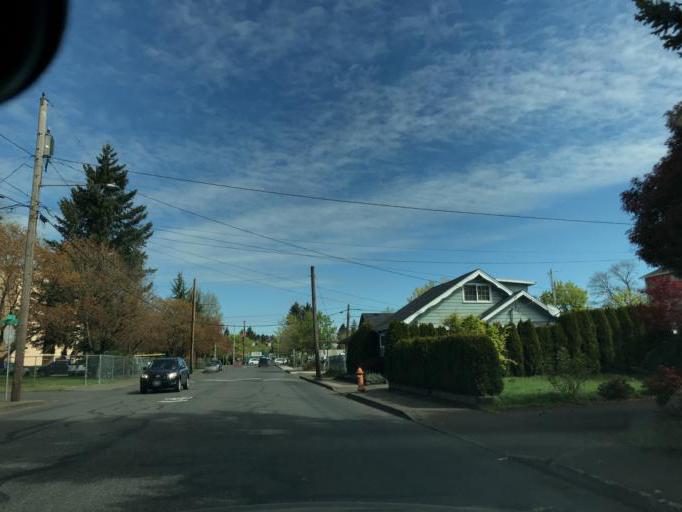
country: US
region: Oregon
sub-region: Multnomah County
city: Lents
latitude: 45.4959
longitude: -122.5740
